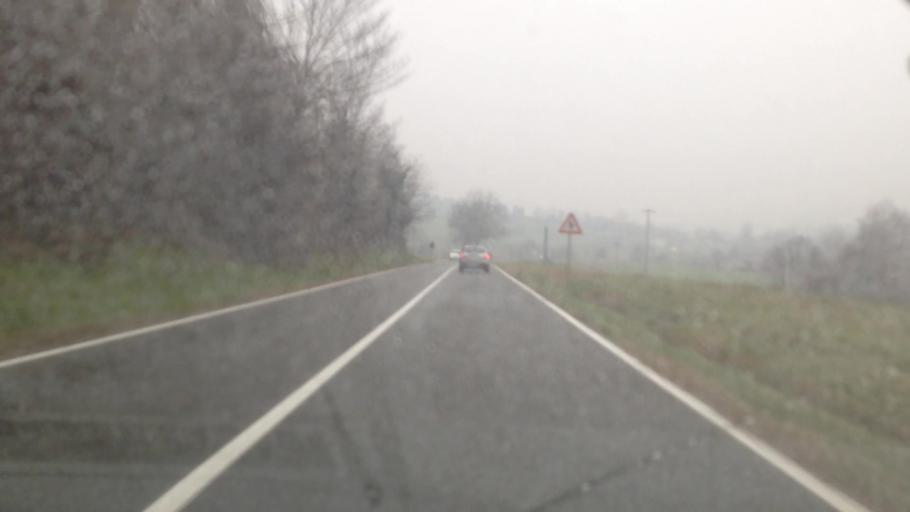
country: IT
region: Piedmont
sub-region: Provincia di Torino
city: Brozolo
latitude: 45.0998
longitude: 8.0807
